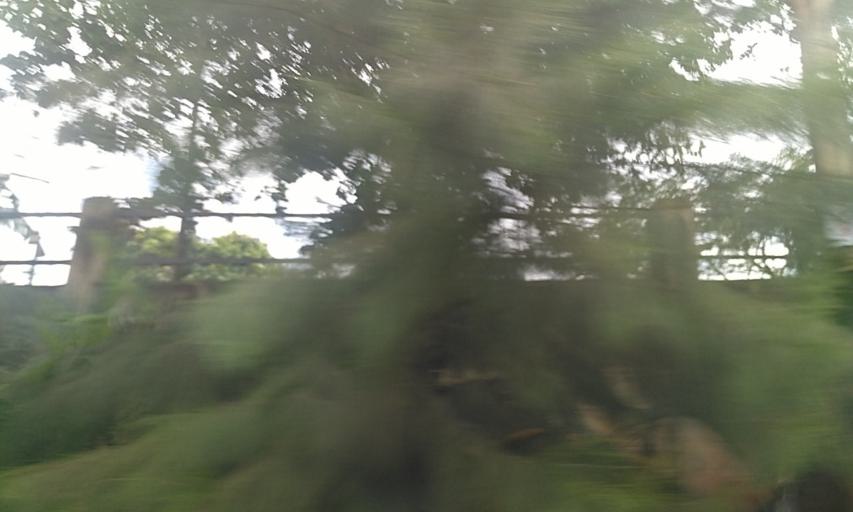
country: UG
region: Central Region
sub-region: Kampala District
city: Kampala
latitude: 0.3239
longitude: 32.5943
